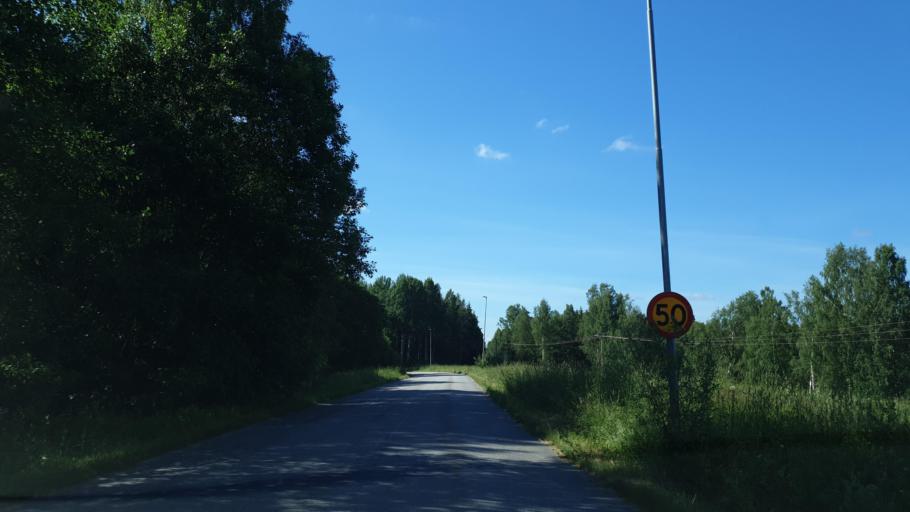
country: SE
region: Dalarna
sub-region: Avesta Kommun
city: Avesta
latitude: 60.1270
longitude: 16.2676
